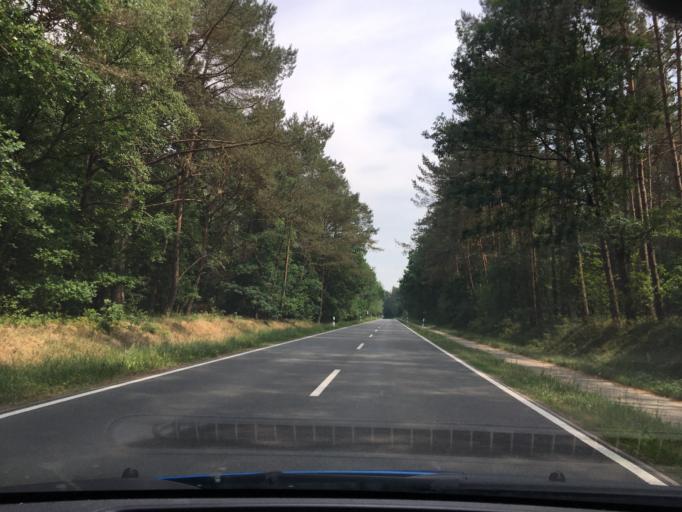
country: DE
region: Lower Saxony
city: Asendorf
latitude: 53.2691
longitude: 9.9570
